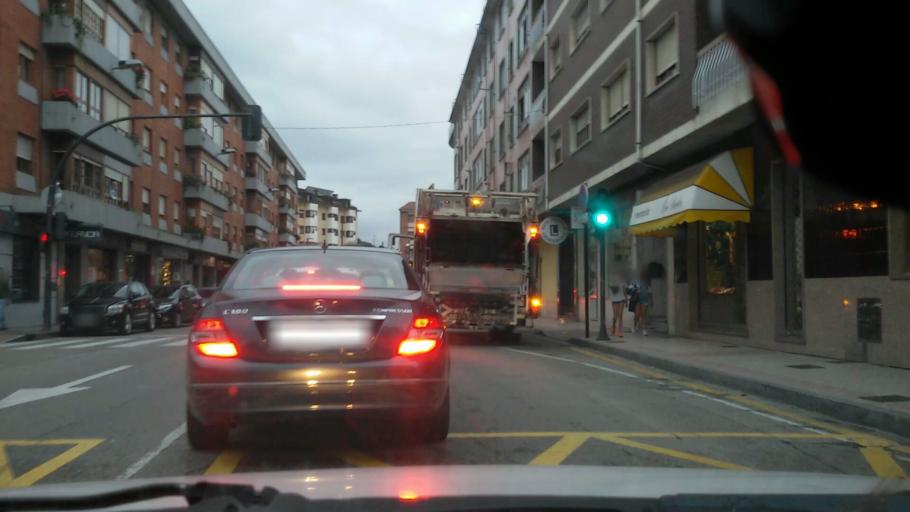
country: ES
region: Asturias
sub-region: Province of Asturias
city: Lugones
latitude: 43.4003
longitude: -5.8098
